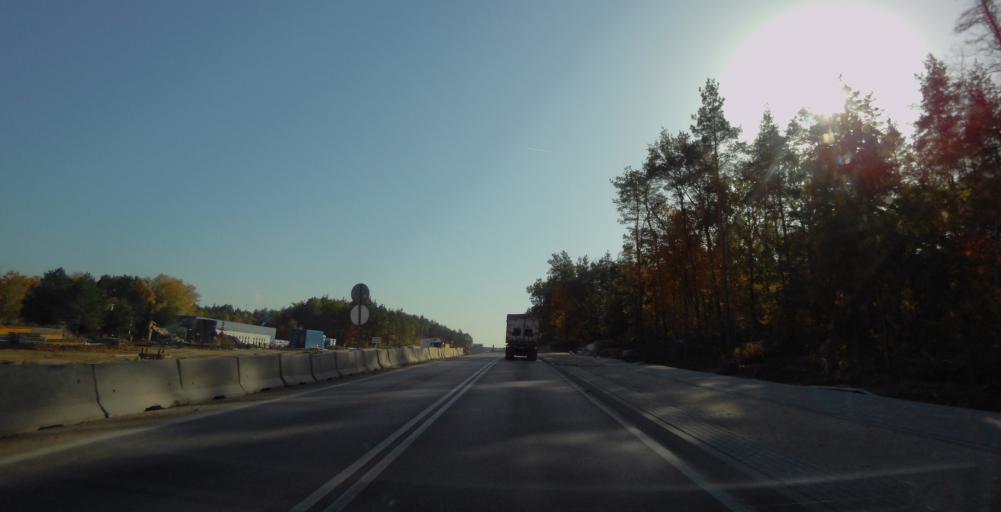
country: PL
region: Masovian Voivodeship
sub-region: Powiat otwocki
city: Jozefow
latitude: 52.1801
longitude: 21.2858
